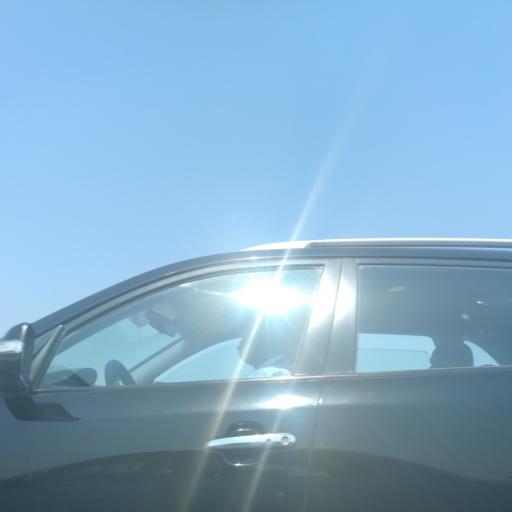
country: NG
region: Abuja Federal Capital Territory
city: Abuja
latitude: 9.0780
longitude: 7.4565
